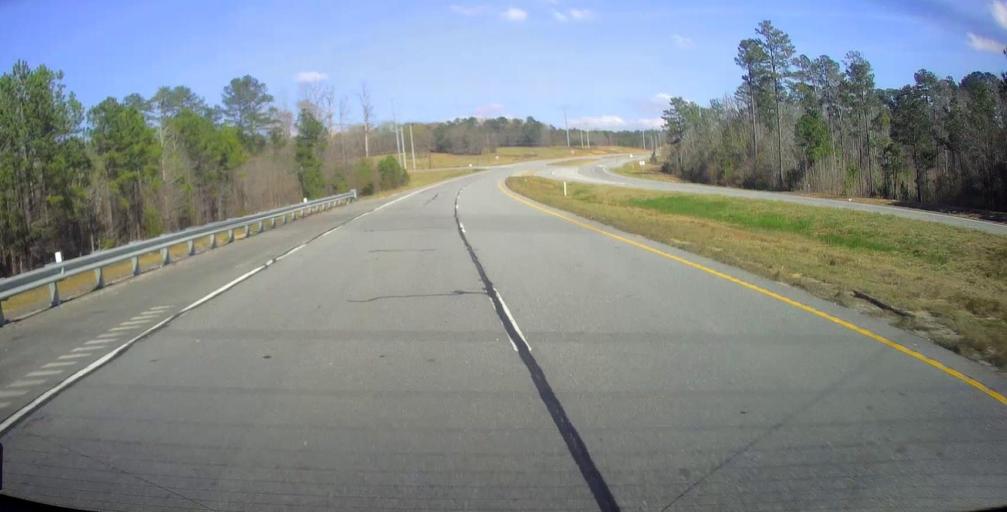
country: US
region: Georgia
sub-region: Wilkinson County
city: Gordon
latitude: 32.9015
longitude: -83.3514
